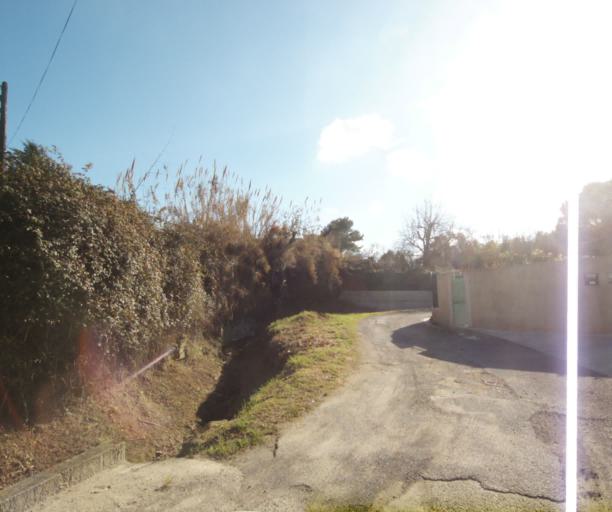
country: FR
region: Provence-Alpes-Cote d'Azur
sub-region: Departement des Alpes-Maritimes
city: Biot
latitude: 43.6045
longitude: 7.1048
